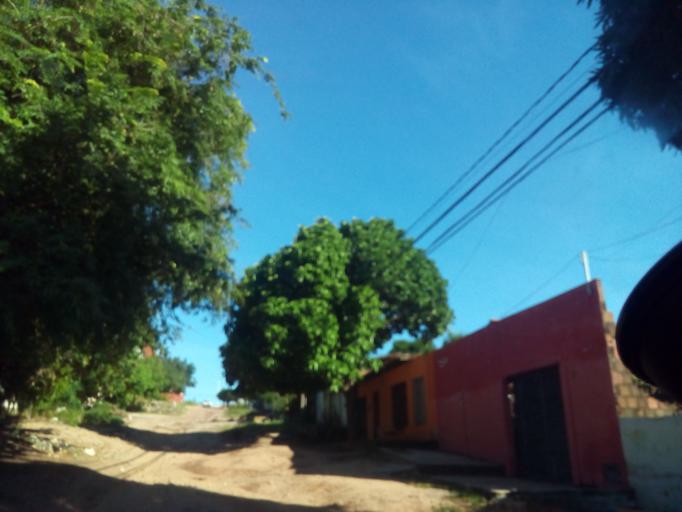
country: BR
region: Rio Grande do Norte
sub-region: Parnamirim
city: Parnamirim
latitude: -5.8659
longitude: -35.2137
